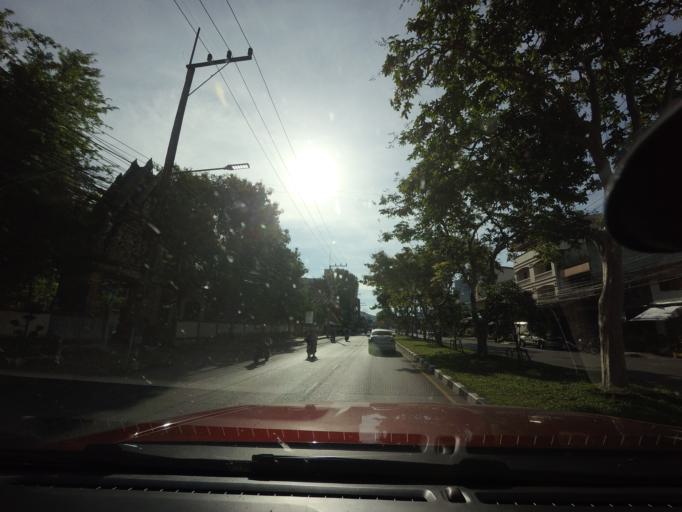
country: TH
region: Songkhla
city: Hat Yai
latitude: 6.9985
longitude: 100.4860
